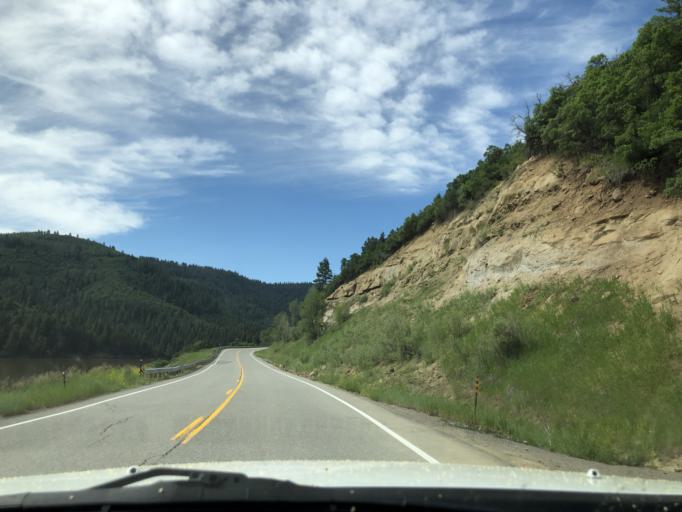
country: US
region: Colorado
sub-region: Delta County
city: Paonia
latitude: 38.9629
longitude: -107.3387
